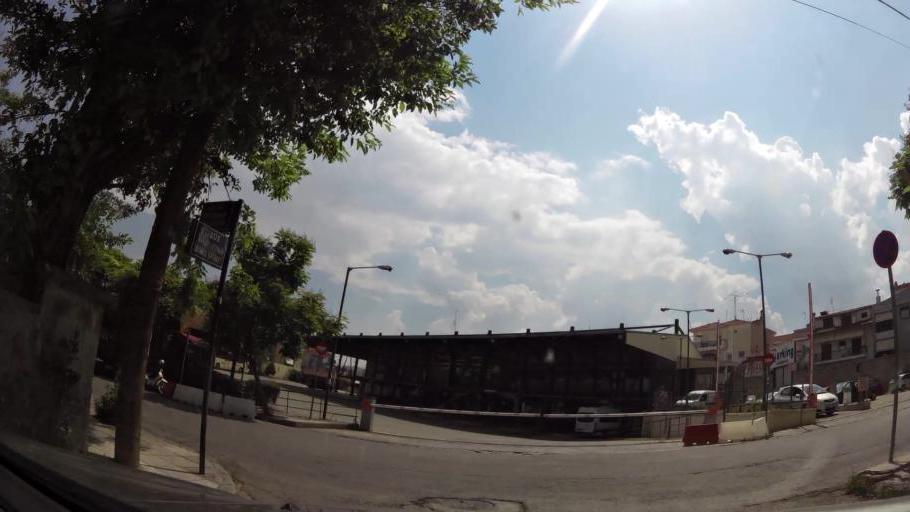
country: GR
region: West Macedonia
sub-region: Nomos Kozanis
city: Kozani
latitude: 40.3008
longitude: 21.7980
